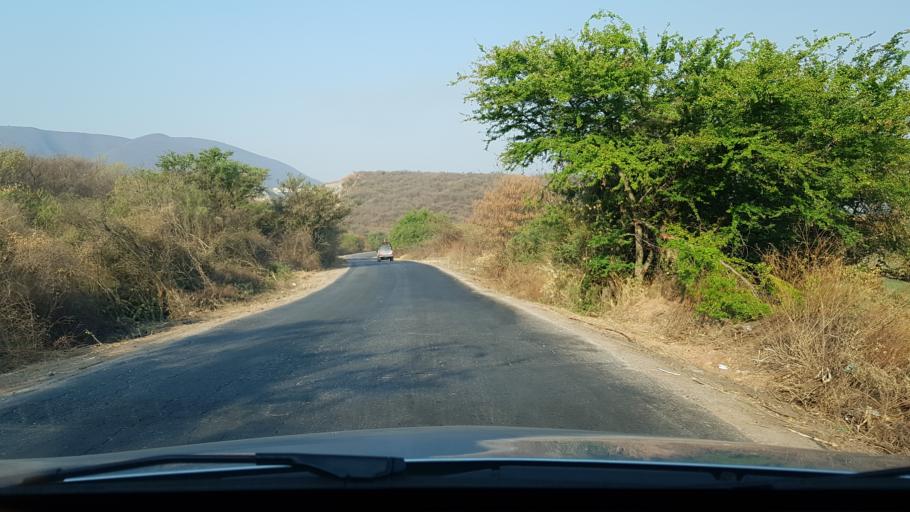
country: MX
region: Morelos
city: Tlaltizapan
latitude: 18.6785
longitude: -99.0839
